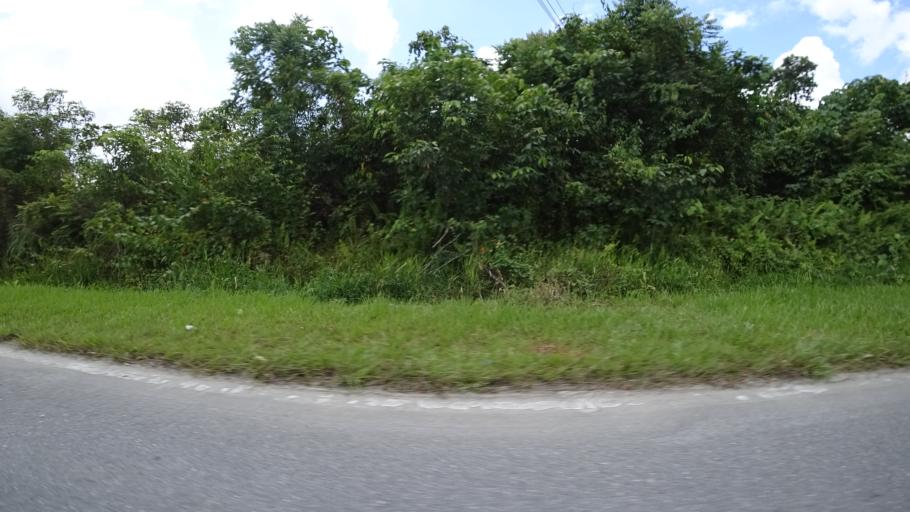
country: BN
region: Tutong
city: Tutong
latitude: 4.6867
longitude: 114.8078
